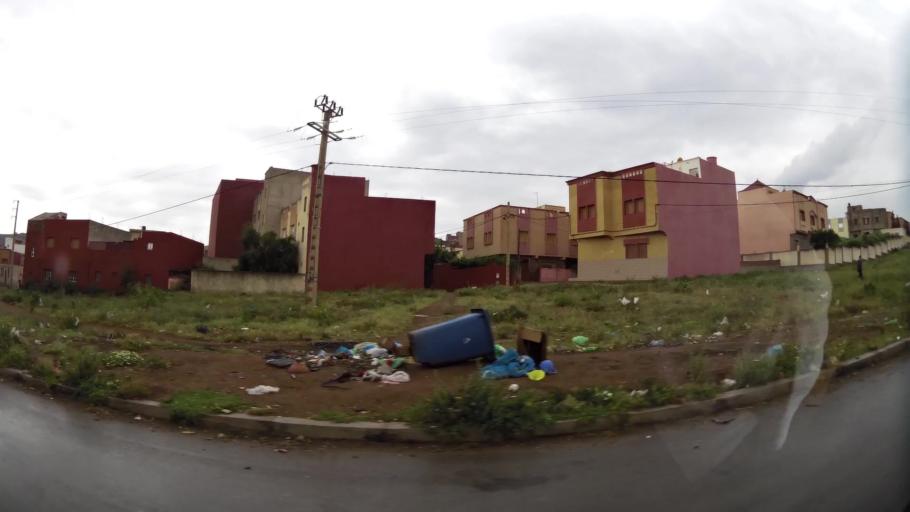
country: MA
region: Oriental
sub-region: Nador
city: Nador
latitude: 35.1499
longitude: -2.9939
